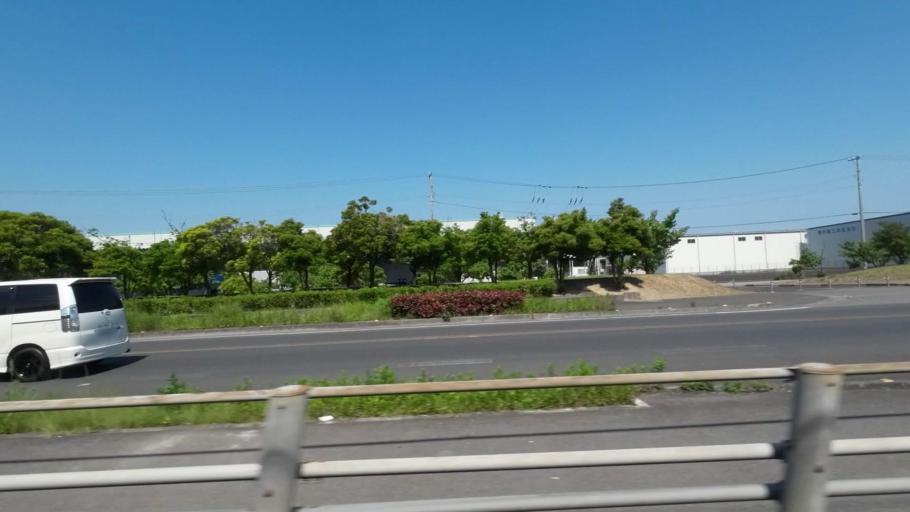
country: JP
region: Ehime
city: Kawanoecho
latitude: 34.0255
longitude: 133.5814
